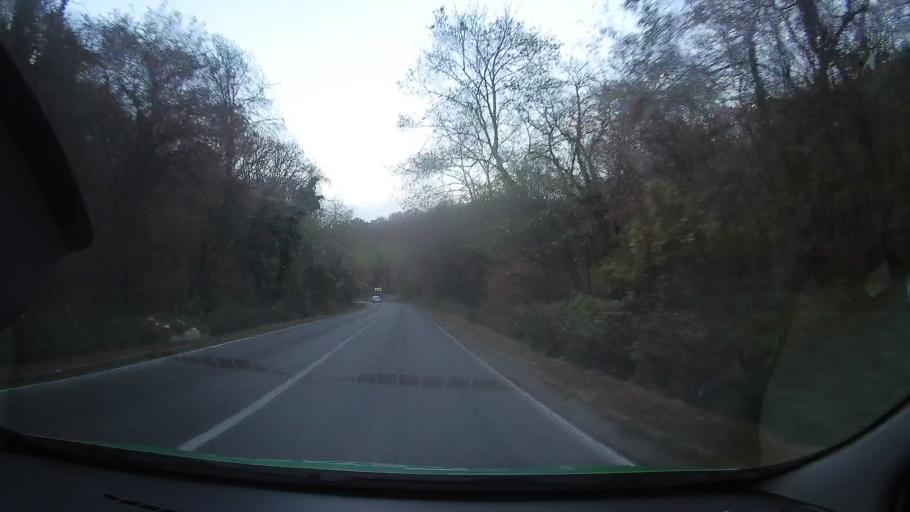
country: RO
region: Constanta
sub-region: Comuna Baneasa
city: Baneasa
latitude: 44.0927
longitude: 27.6534
